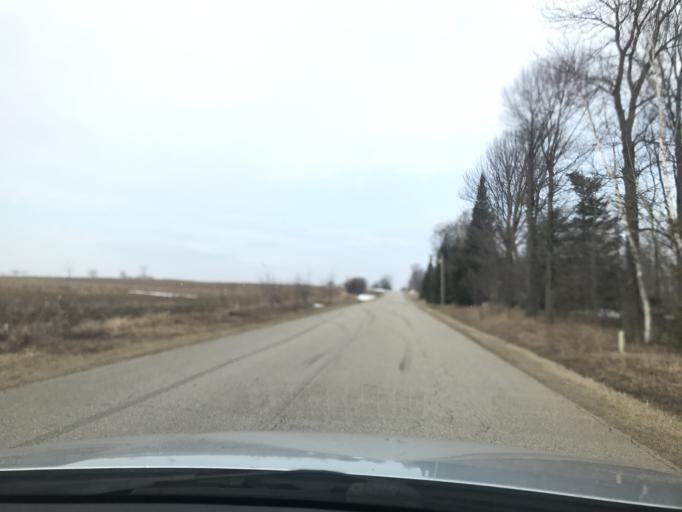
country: US
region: Wisconsin
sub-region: Oconto County
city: Oconto Falls
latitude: 44.8505
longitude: -88.1541
